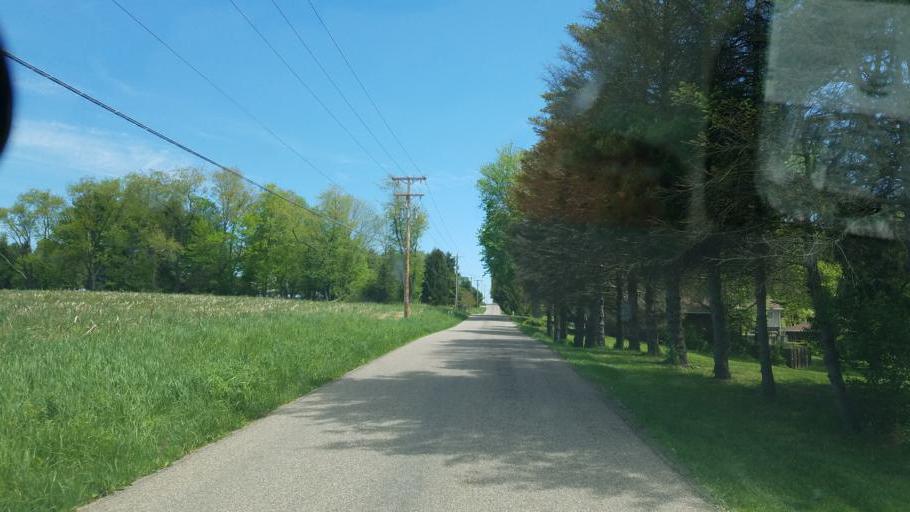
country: US
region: Ohio
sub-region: Knox County
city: Gambier
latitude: 40.3891
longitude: -82.3856
